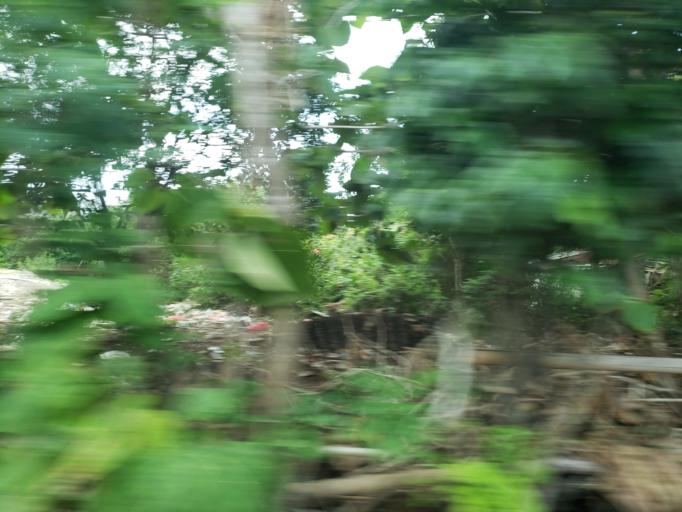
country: ID
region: Bali
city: Kangin
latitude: -8.8400
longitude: 115.1526
